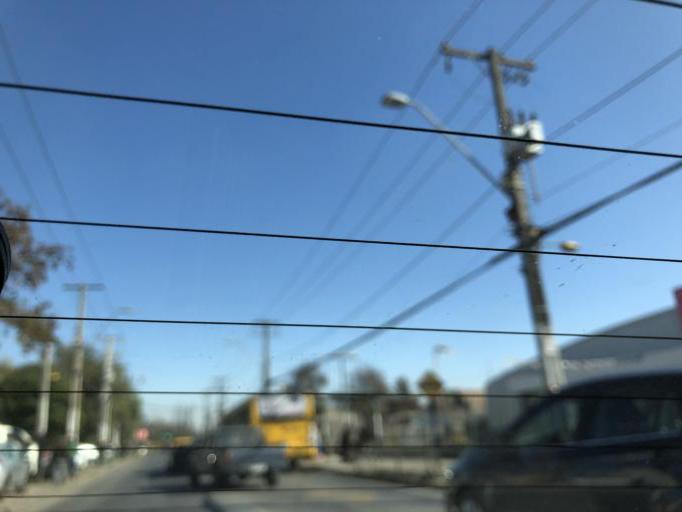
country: CL
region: Santiago Metropolitan
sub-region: Provincia de Santiago
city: La Pintana
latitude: -33.6184
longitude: -70.6252
